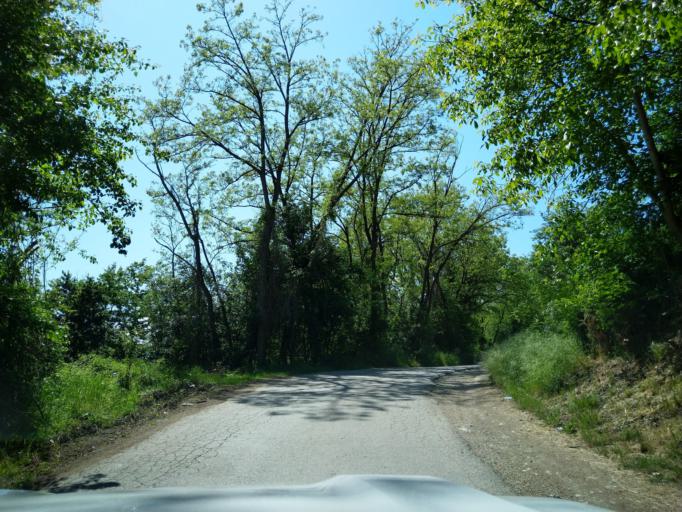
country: RS
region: Central Serbia
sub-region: Zlatiborski Okrug
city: Pozega
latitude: 43.8635
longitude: 19.9459
